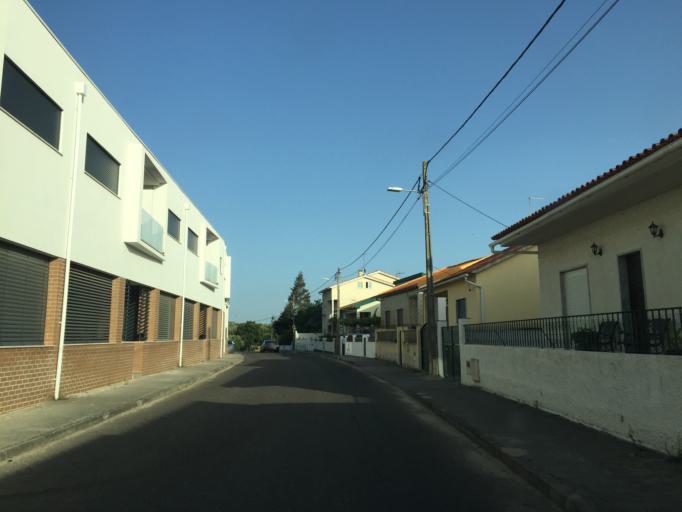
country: PT
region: Santarem
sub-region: Chamusca
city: Vila Nova da Barquinha
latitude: 39.4673
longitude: -8.4401
